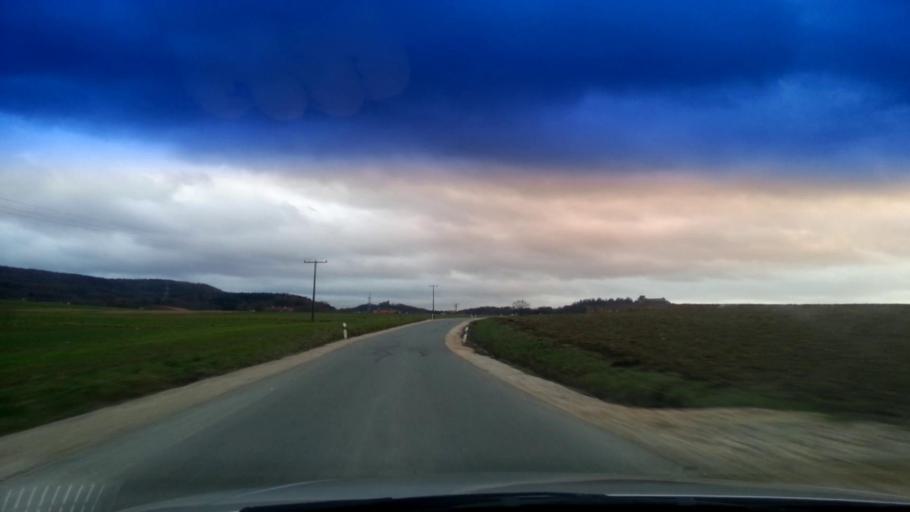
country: DE
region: Bavaria
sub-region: Upper Franconia
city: Schesslitz
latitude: 49.9762
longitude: 11.0587
